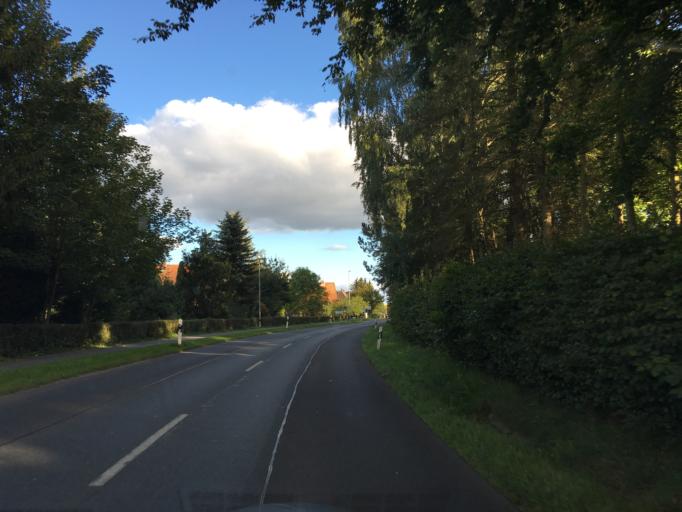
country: DE
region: Lower Saxony
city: Reppenstedt
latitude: 53.2476
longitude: 10.3659
